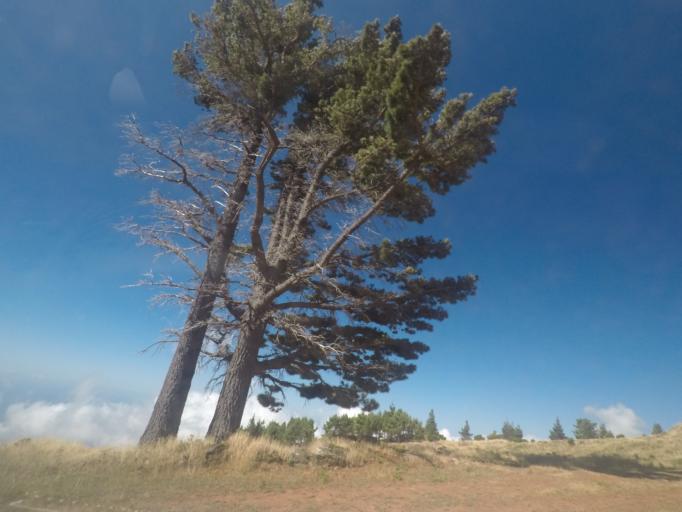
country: PT
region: Madeira
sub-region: Funchal
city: Nossa Senhora do Monte
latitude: 32.7064
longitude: -16.9067
